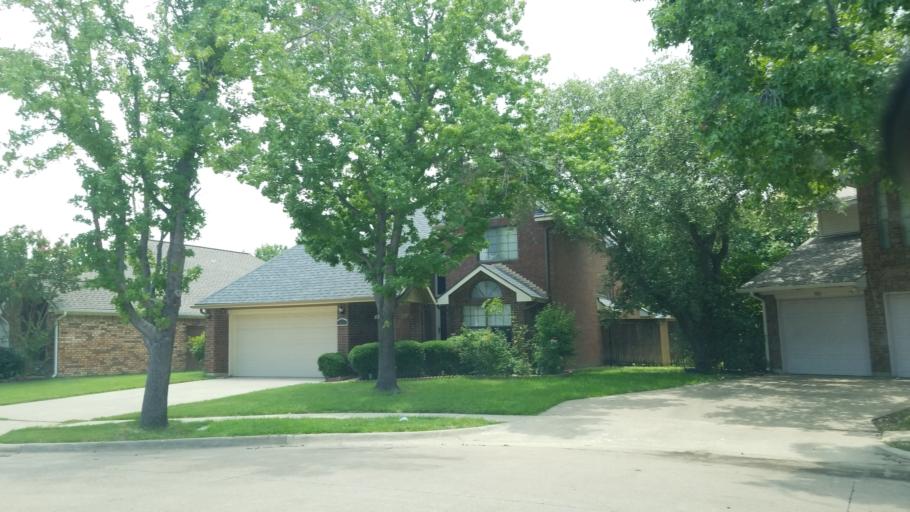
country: US
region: Texas
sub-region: Dallas County
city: Farmers Branch
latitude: 32.9367
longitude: -96.9536
